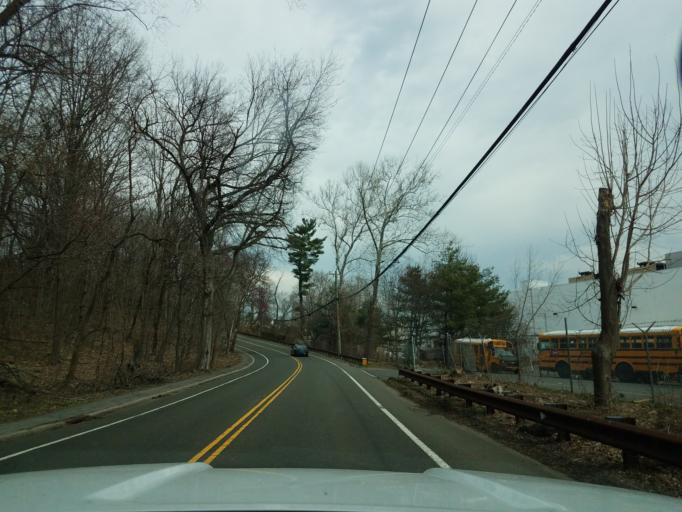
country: US
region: Connecticut
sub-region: Fairfield County
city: Riverside
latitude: 41.0464
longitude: -73.5661
